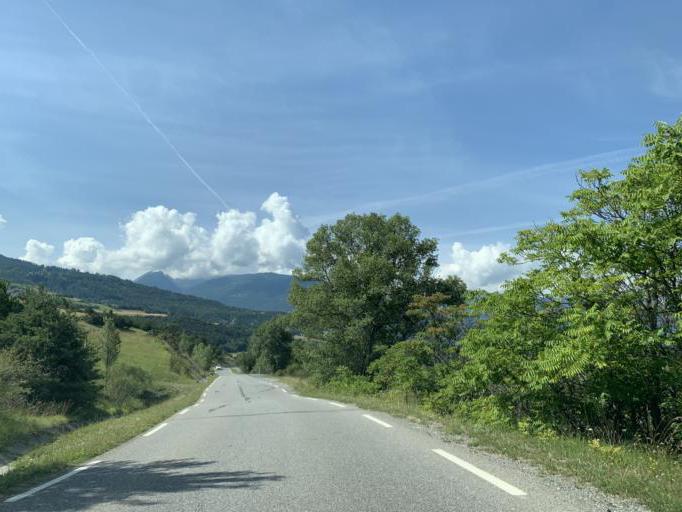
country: FR
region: Provence-Alpes-Cote d'Azur
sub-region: Departement des Hautes-Alpes
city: Embrun
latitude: 44.5722
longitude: 6.5230
